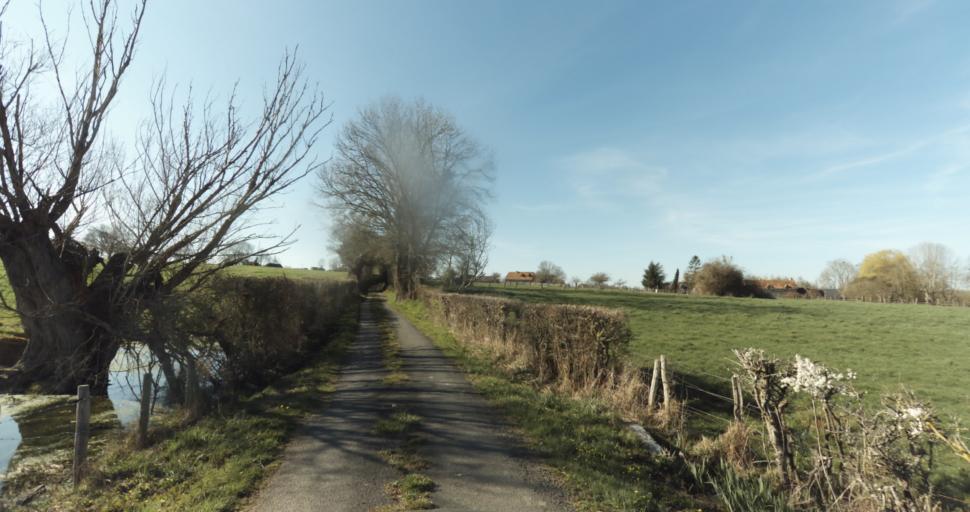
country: FR
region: Lower Normandy
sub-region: Departement du Calvados
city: Livarot
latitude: 49.0292
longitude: 0.0621
